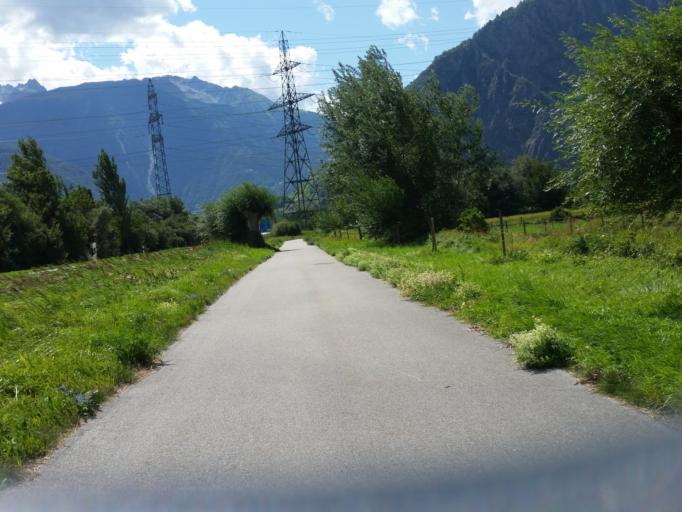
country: CH
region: Valais
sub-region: Martigny District
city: Martigny-Ville
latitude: 46.1183
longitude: 7.0811
